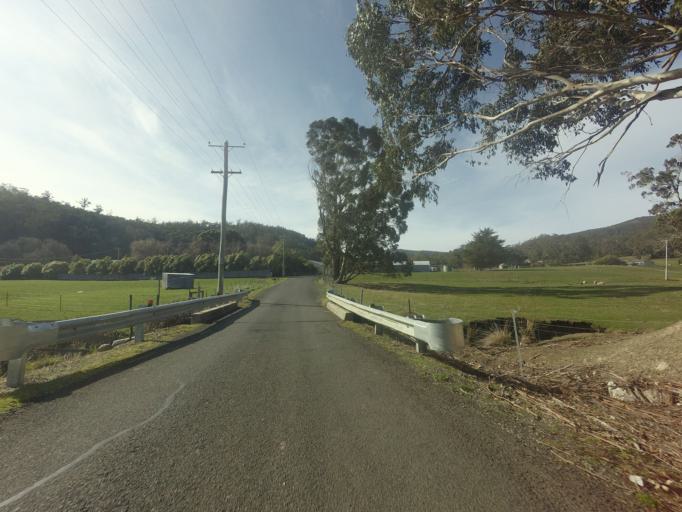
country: AU
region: Tasmania
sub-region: Huon Valley
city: Cygnet
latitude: -43.1797
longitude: 147.1319
